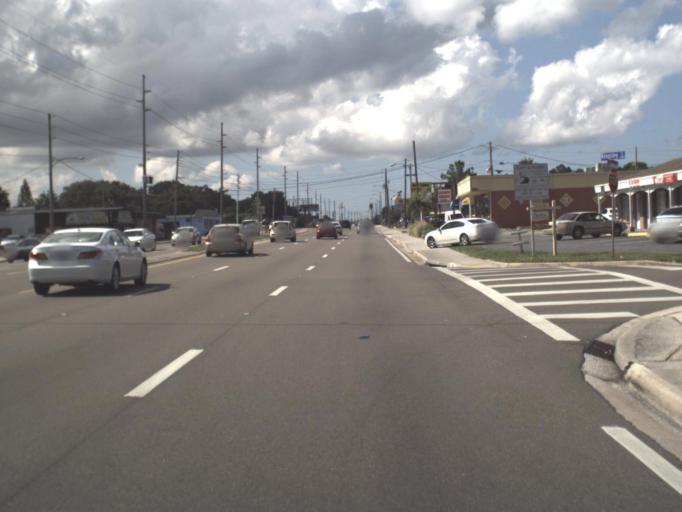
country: US
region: Florida
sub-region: Pinellas County
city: Belleair
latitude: 27.9464
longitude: -82.7876
